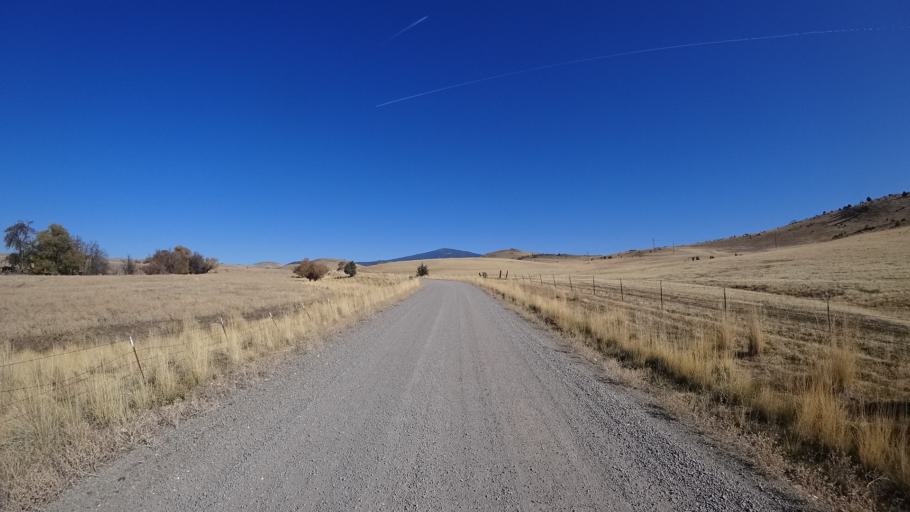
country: US
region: California
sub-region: Siskiyou County
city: Montague
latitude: 41.7456
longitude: -122.3643
